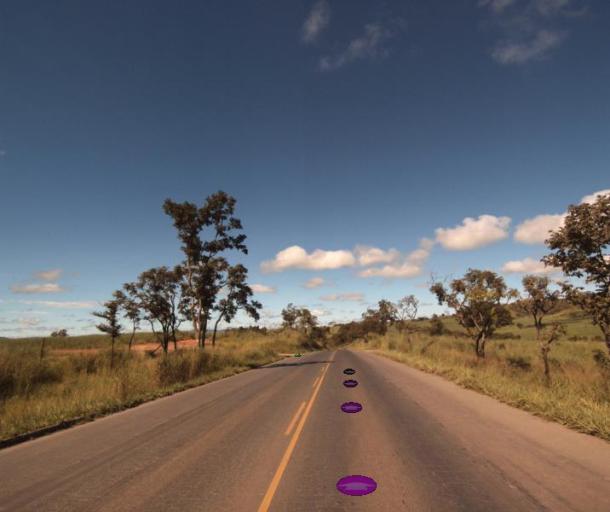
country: BR
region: Goias
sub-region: Itapaci
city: Itapaci
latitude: -15.0814
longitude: -49.4633
